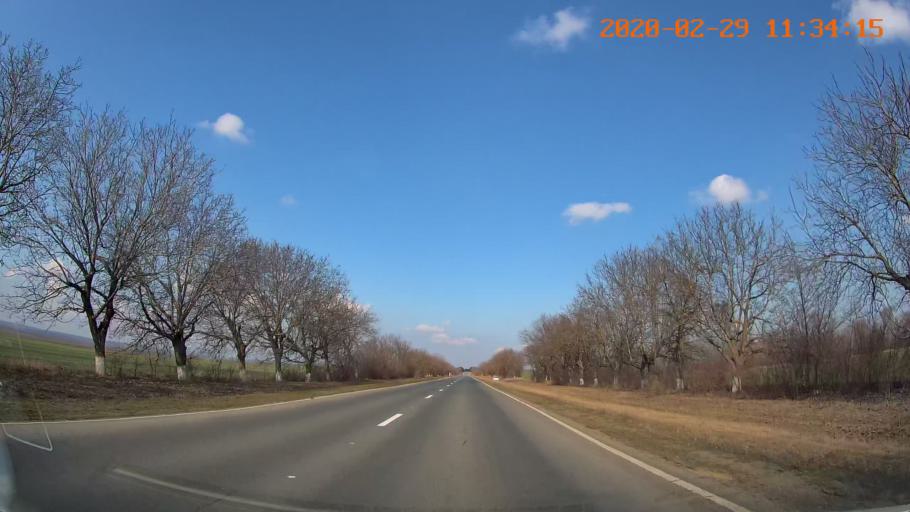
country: MD
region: Rezina
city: Saharna
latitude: 47.5631
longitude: 29.0758
